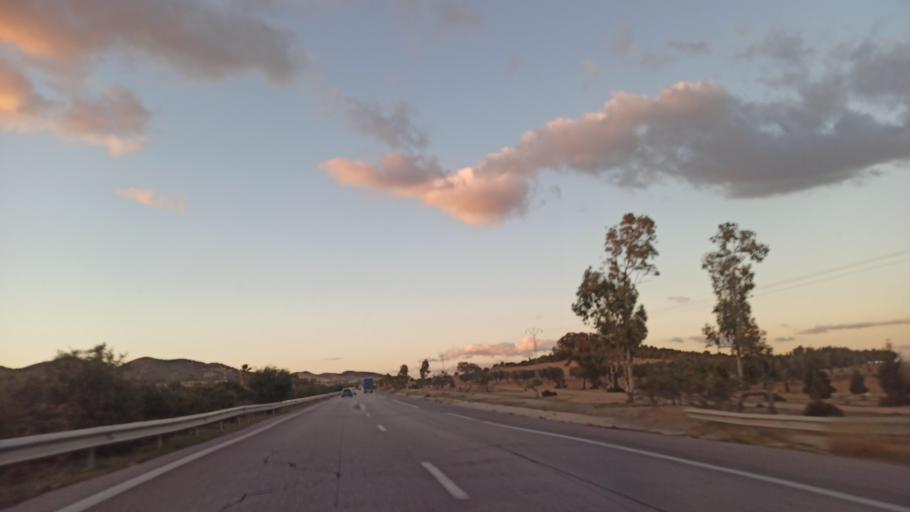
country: TN
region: Susah
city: Harqalah
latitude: 36.2181
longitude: 10.4192
